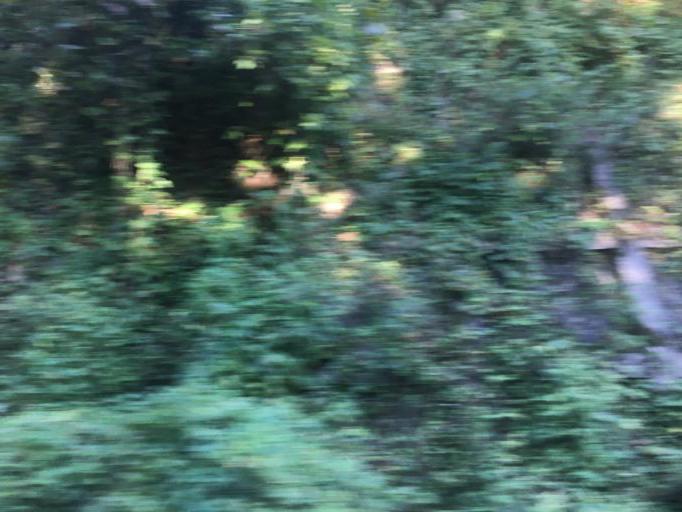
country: JP
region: Akita
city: Takanosu
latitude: 39.9918
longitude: 140.4023
